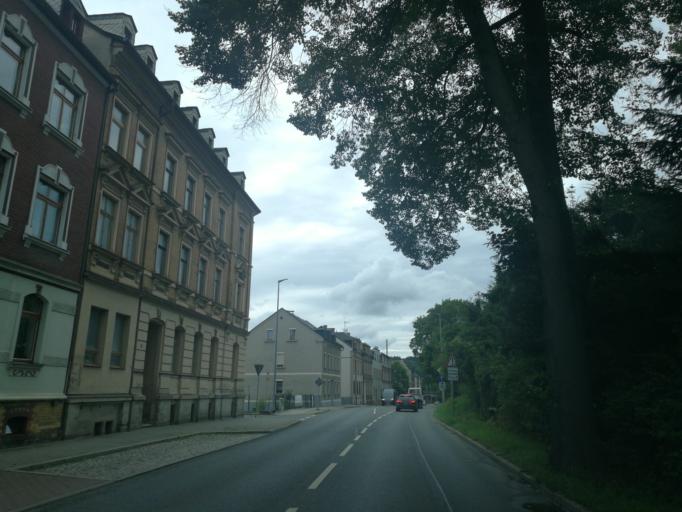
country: DE
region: Saxony
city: Adorf
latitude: 50.3194
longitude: 12.2652
